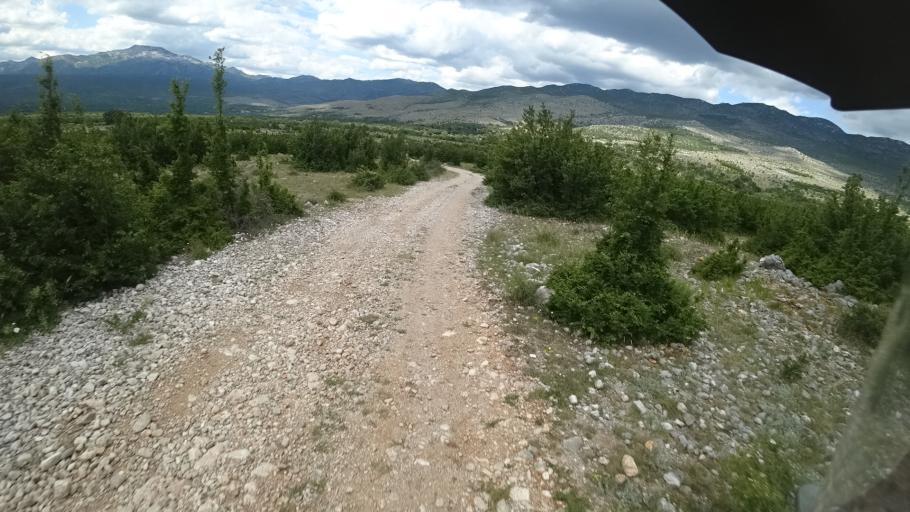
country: HR
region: Zadarska
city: Gracac
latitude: 44.1713
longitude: 15.9230
